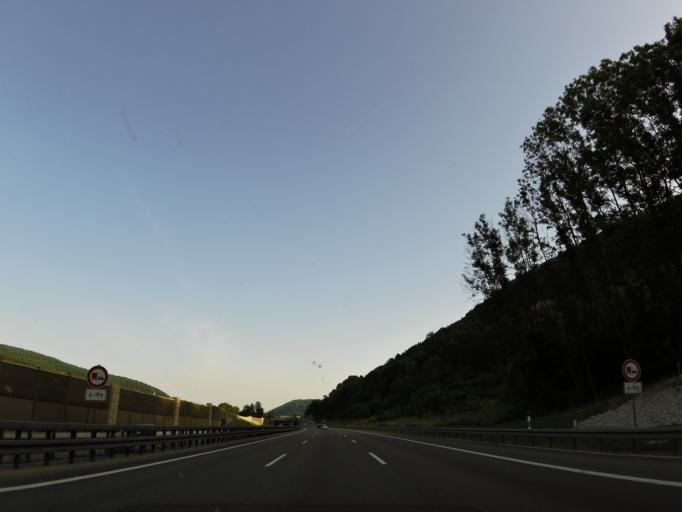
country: DE
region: Baden-Wuerttemberg
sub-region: Regierungsbezirk Stuttgart
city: Gruibingen
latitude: 48.5917
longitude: 9.6498
